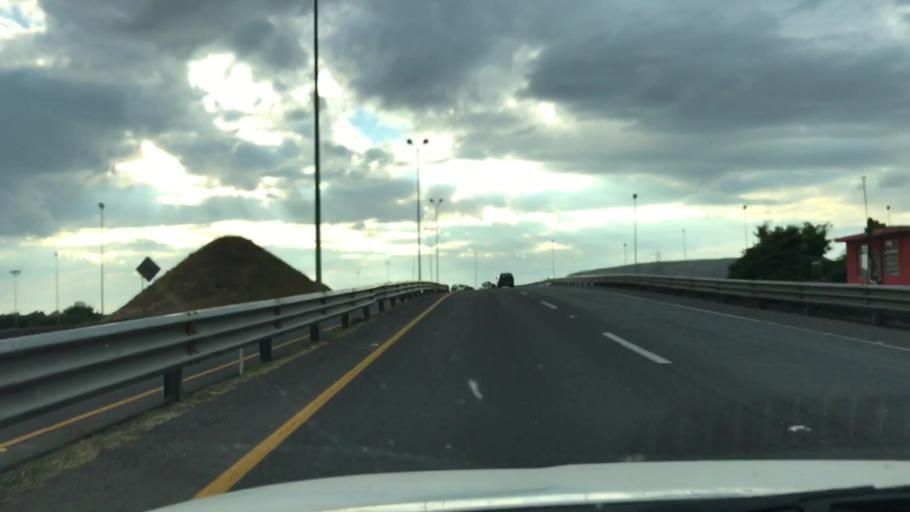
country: MX
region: Guanajuato
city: Penjamo
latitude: 20.4194
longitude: -101.7230
